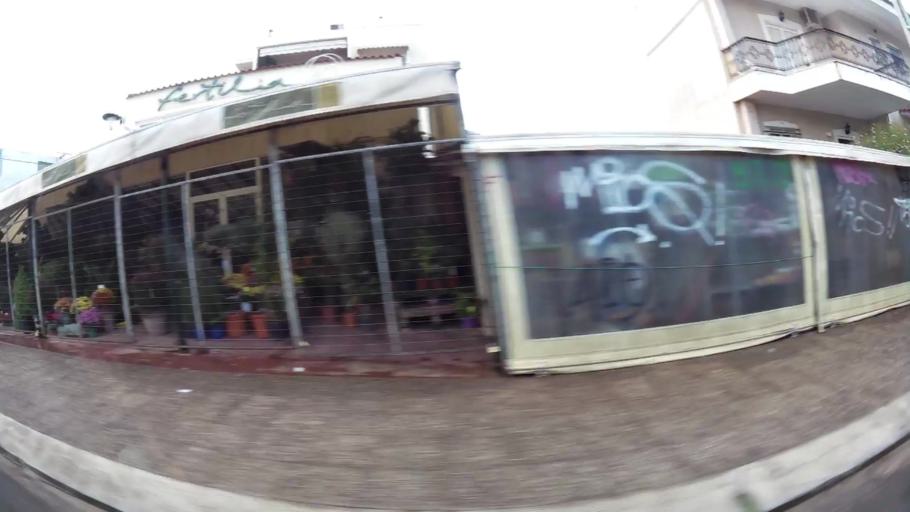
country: GR
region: Attica
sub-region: Nomarchia Athinas
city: Marousi
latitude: 38.0430
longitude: 23.8143
